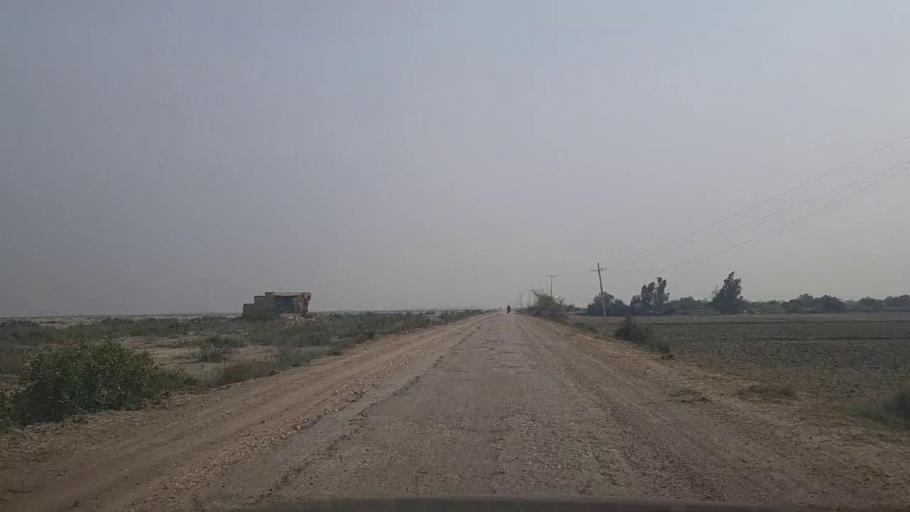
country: PK
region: Sindh
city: Mirpur Sakro
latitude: 24.4695
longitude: 67.6772
